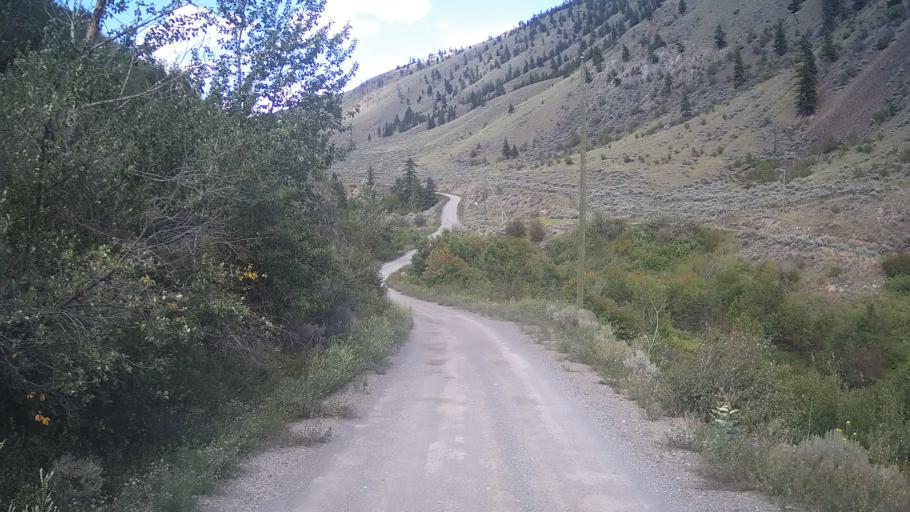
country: CA
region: British Columbia
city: Lillooet
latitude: 51.2002
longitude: -122.1011
